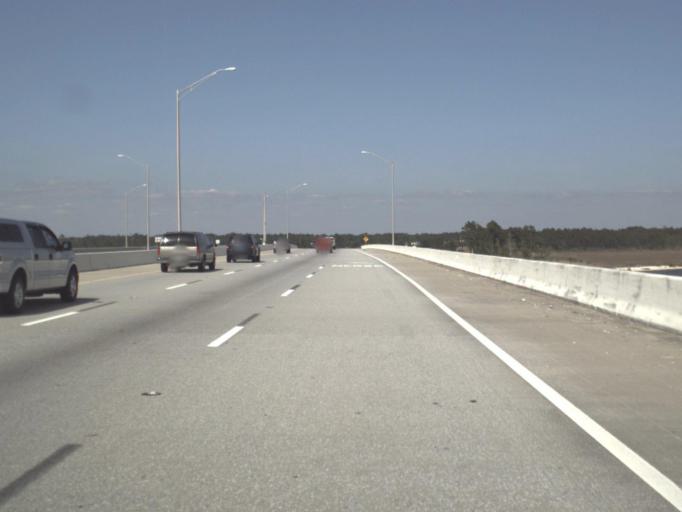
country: US
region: Florida
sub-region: Santa Rosa County
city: Pace
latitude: 30.5288
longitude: -87.1304
